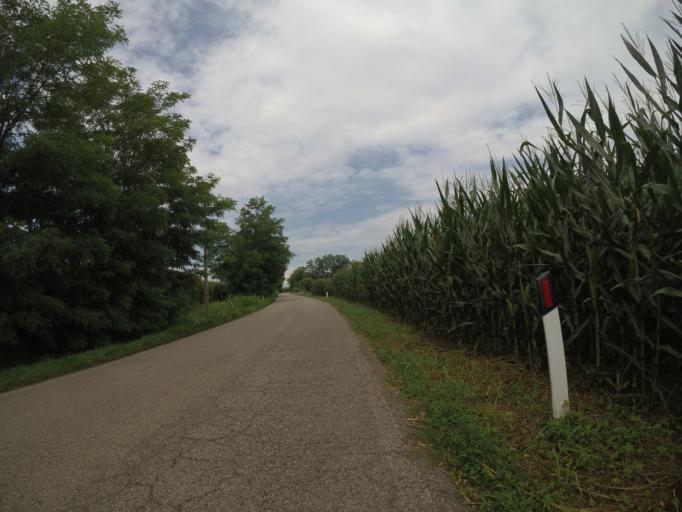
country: IT
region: Friuli Venezia Giulia
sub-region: Provincia di Udine
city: Lestizza
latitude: 45.9736
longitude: 13.1029
